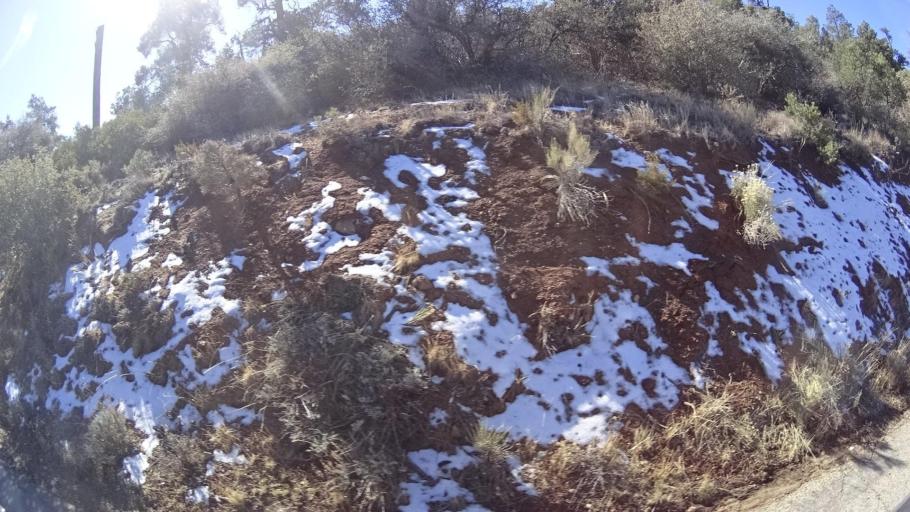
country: US
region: California
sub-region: Kern County
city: Pine Mountain Club
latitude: 34.8661
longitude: -119.2538
